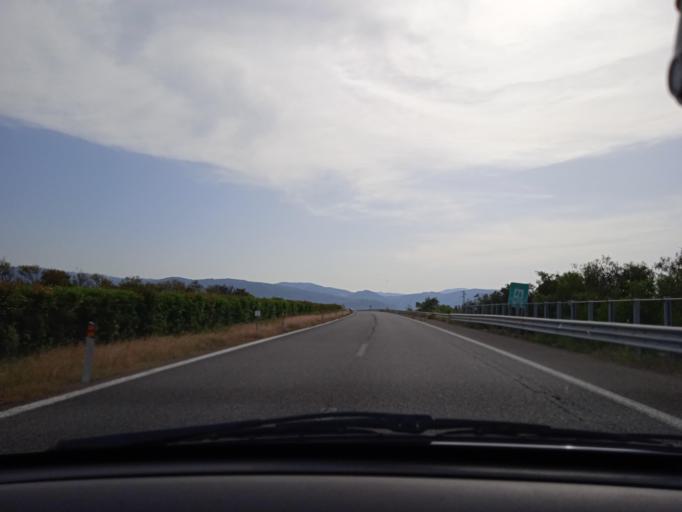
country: IT
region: Sicily
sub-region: Messina
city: Vigliatore 2
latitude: 38.1335
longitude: 15.1390
